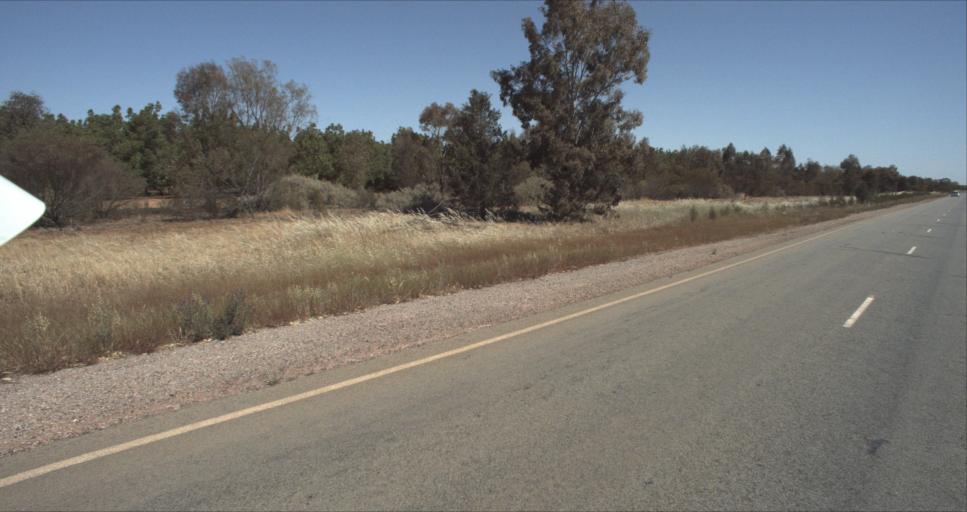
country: AU
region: New South Wales
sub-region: Leeton
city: Leeton
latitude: -34.4988
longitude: 146.4514
